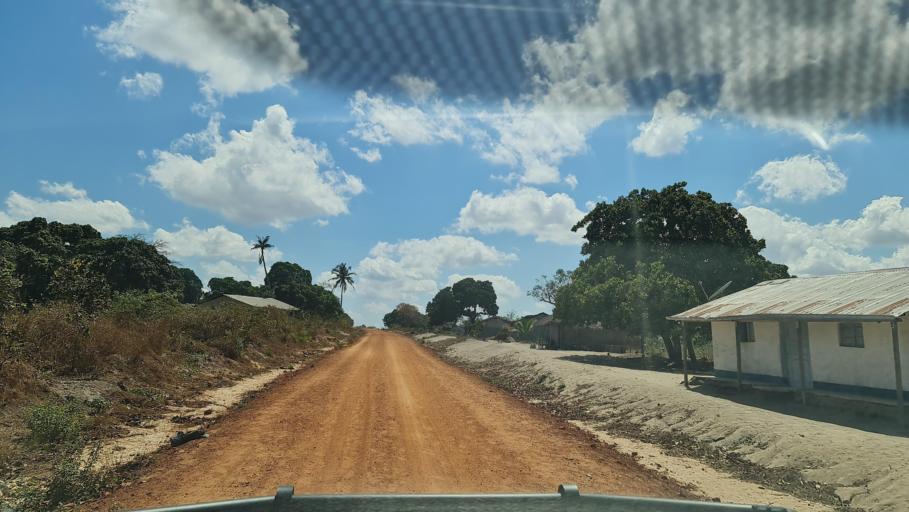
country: MZ
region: Nampula
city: Nacala
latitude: -14.1722
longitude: 40.2440
